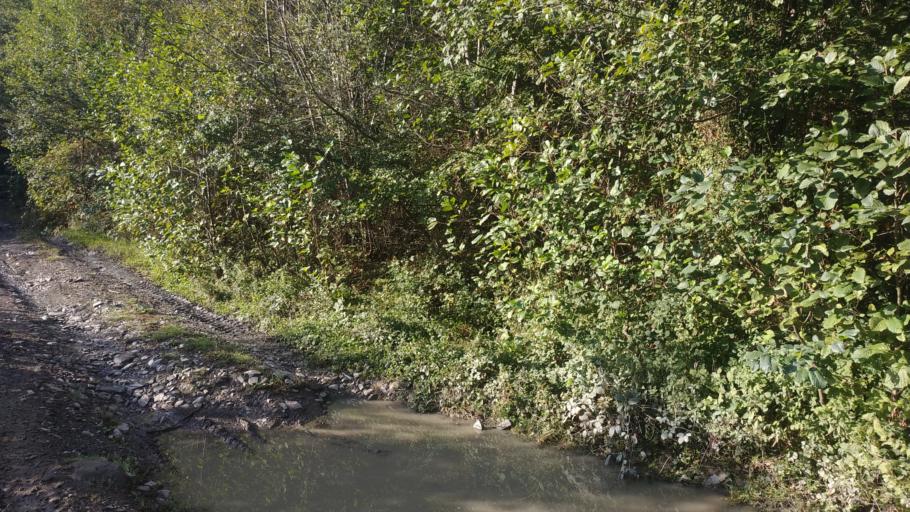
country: RU
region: Krasnodarskiy
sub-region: Sochi City
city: Lazarevskoye
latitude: 43.9952
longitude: 39.3798
